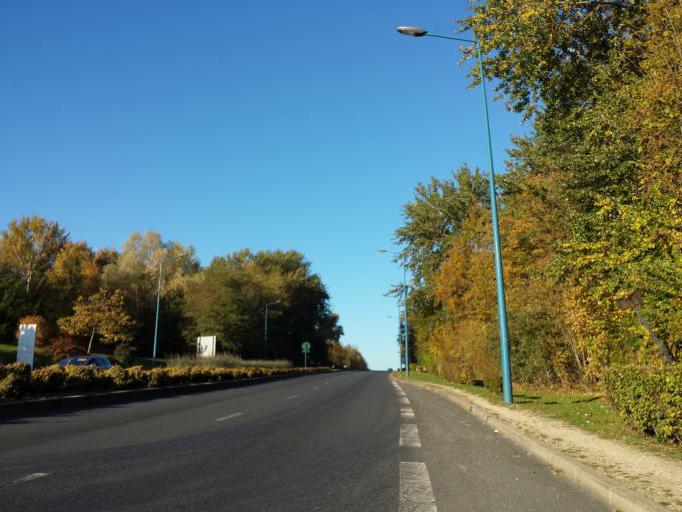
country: FR
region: Ile-de-France
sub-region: Departement du Val-d'Oise
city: Ecouen
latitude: 49.0120
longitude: 2.3846
